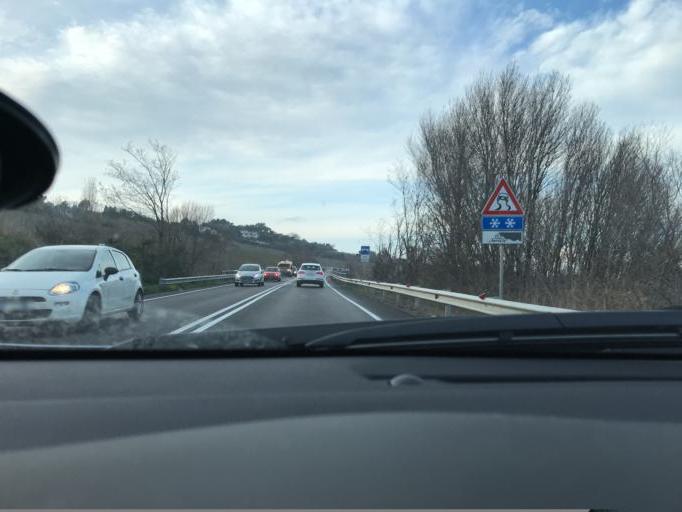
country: IT
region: The Marches
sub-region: Provincia di Ancona
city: Falconara Marittima
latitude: 43.6044
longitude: 13.4211
